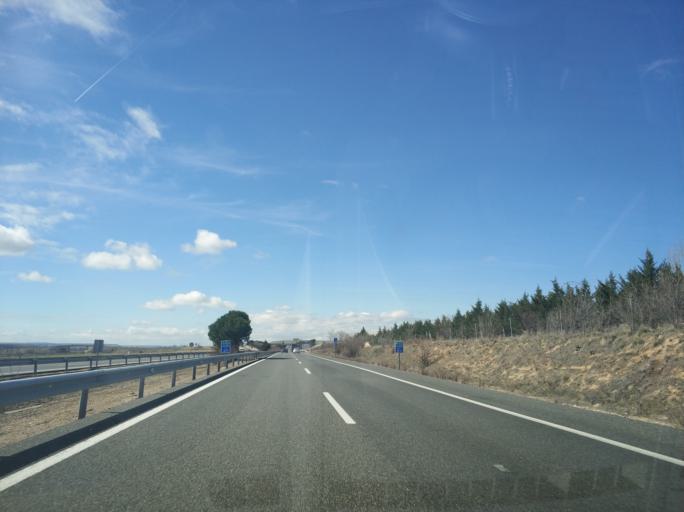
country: ES
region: Castille and Leon
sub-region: Provincia de Burgos
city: Villaldemiro
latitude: 42.2406
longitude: -3.9746
